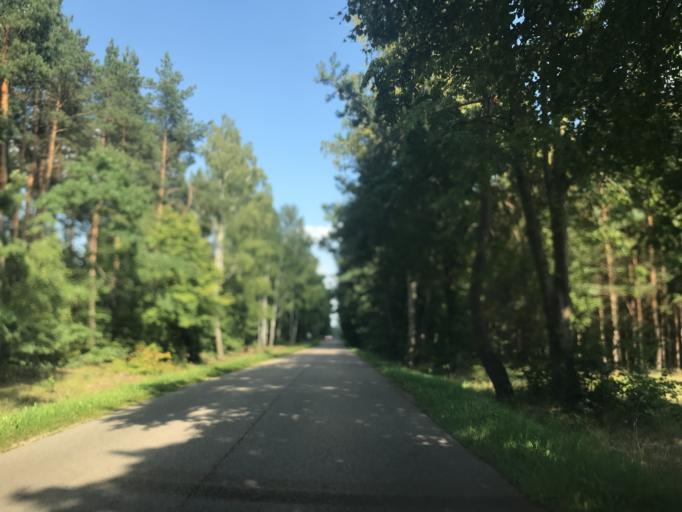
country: PL
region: Masovian Voivodeship
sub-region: Powiat mlawski
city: Wisniewo
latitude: 53.1110
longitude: 20.3151
